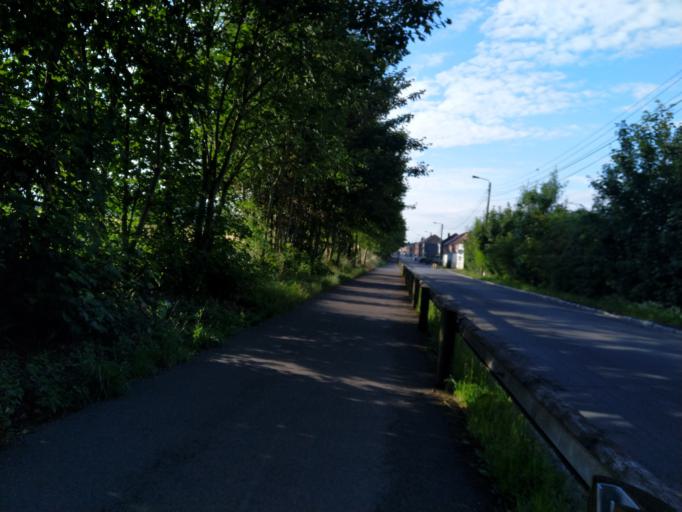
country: BE
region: Wallonia
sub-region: Province du Hainaut
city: Binche
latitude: 50.4410
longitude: 4.1453
